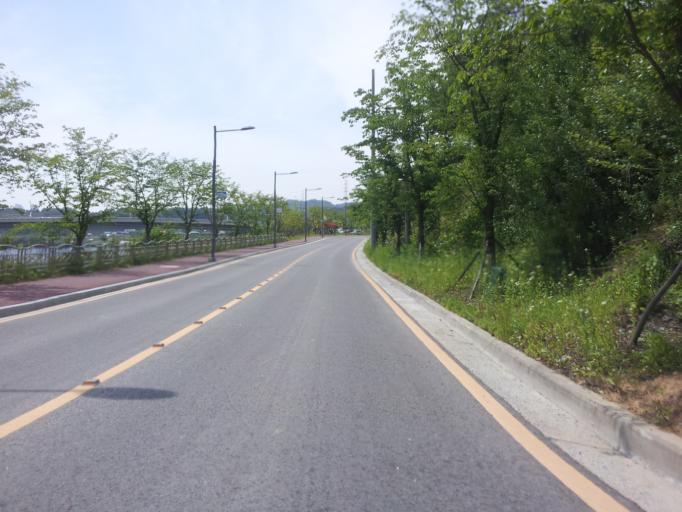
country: KR
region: Daejeon
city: Sintansin
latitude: 36.4576
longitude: 127.4677
